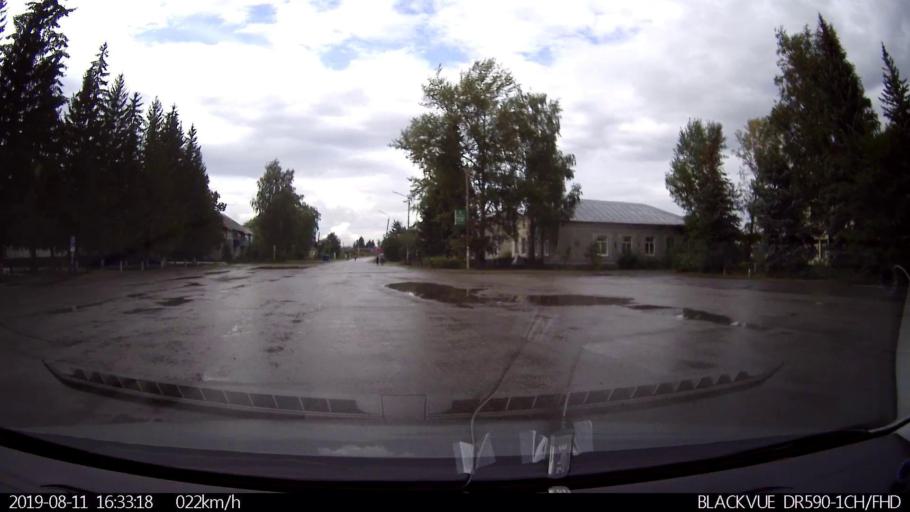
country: RU
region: Ulyanovsk
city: Mayna
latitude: 54.1143
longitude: 47.6261
